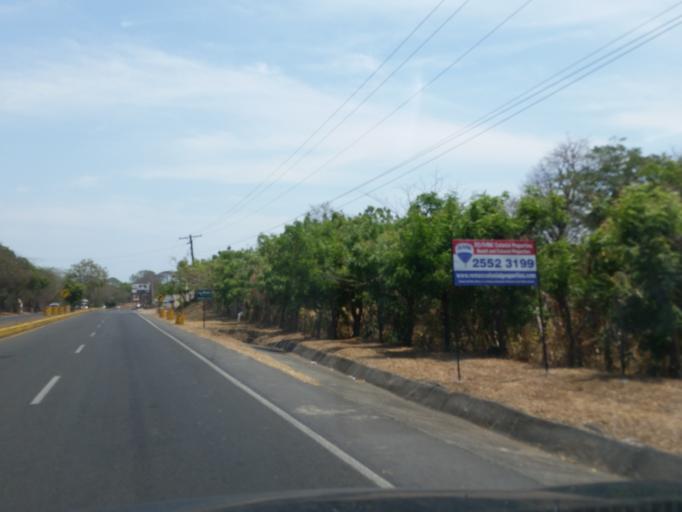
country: NI
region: Granada
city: Granada
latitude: 11.9618
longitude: -85.9994
